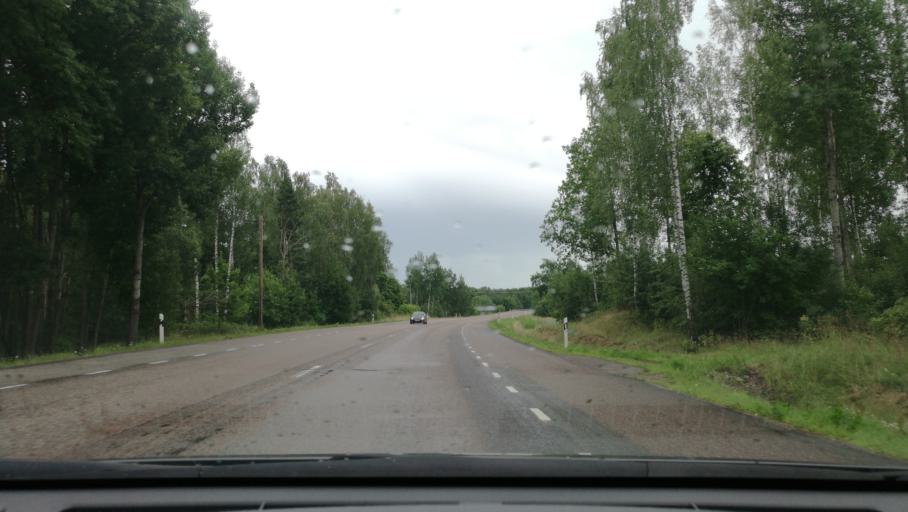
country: SE
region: Vaestmanland
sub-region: Kopings Kommun
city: Koping
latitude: 59.4809
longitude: 15.9869
